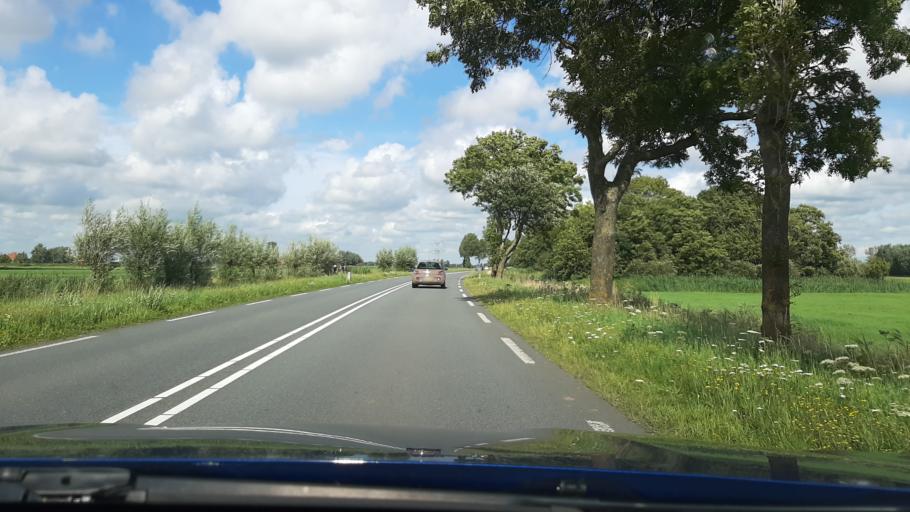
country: NL
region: North Holland
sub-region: Gemeente Zaanstad
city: Zaanstad
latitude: 52.4422
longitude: 4.7377
